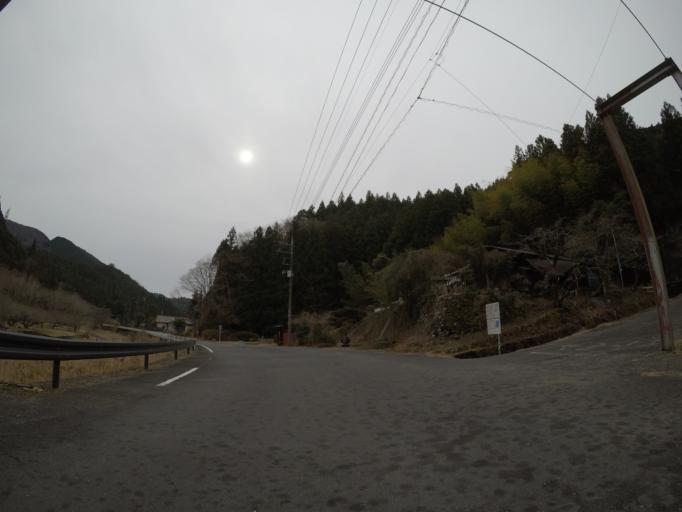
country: JP
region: Shizuoka
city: Fujinomiya
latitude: 35.2735
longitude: 138.5290
